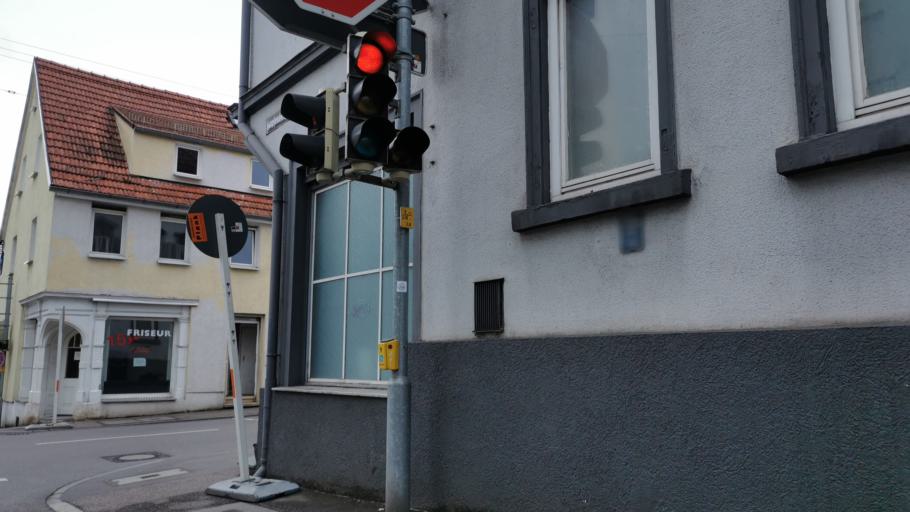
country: DE
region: Baden-Wuerttemberg
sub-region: Regierungsbezirk Stuttgart
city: Stuttgart Feuerbach
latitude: 48.8061
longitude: 9.1559
